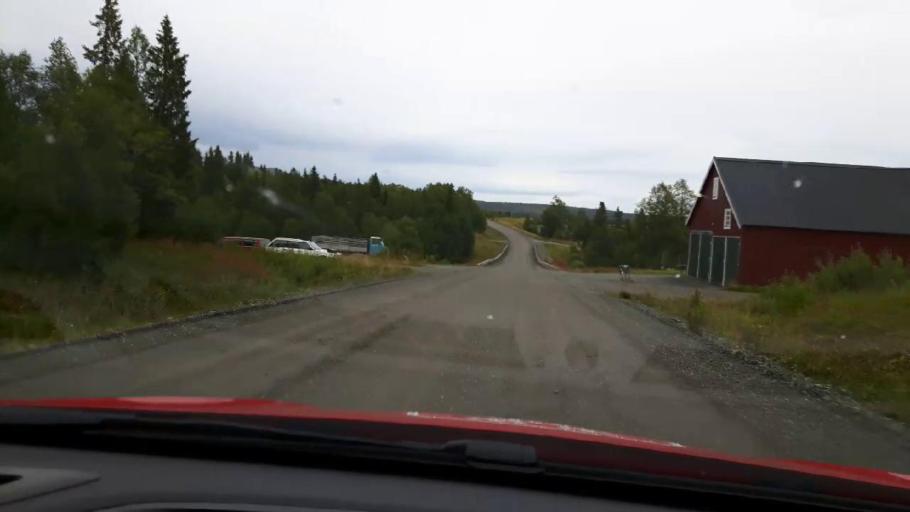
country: NO
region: Nord-Trondelag
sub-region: Meraker
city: Meraker
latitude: 63.5581
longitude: 12.3383
